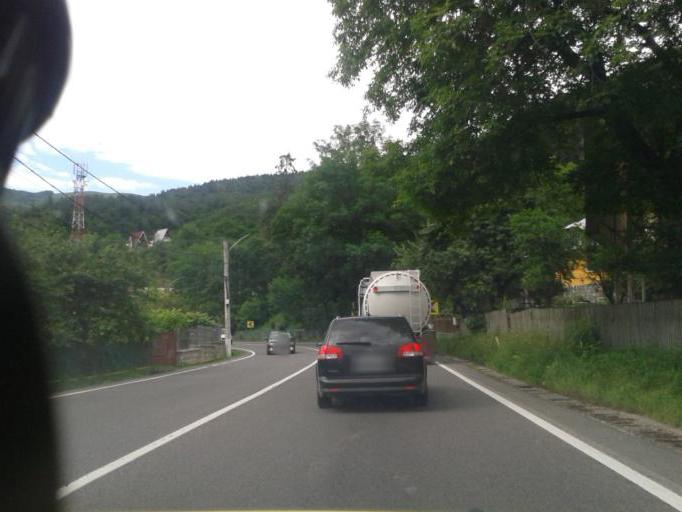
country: RO
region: Prahova
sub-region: Comuna Comarnic
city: Posada
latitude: 45.2841
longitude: 25.6190
